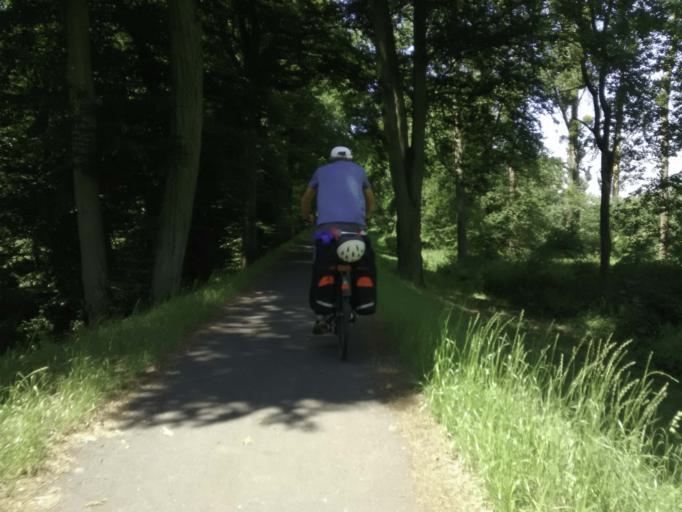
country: DE
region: Saxony-Anhalt
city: Vockerode
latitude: 51.8639
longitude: 12.3294
